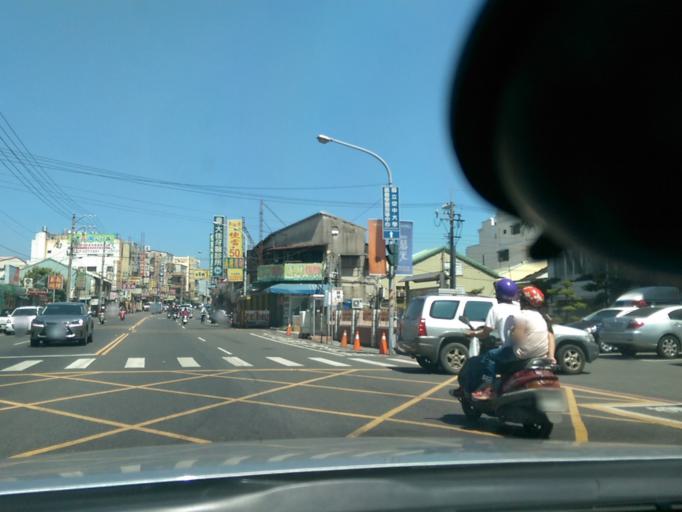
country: TW
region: Taiwan
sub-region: Chiayi
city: Jiayi Shi
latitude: 23.4637
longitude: 120.4556
